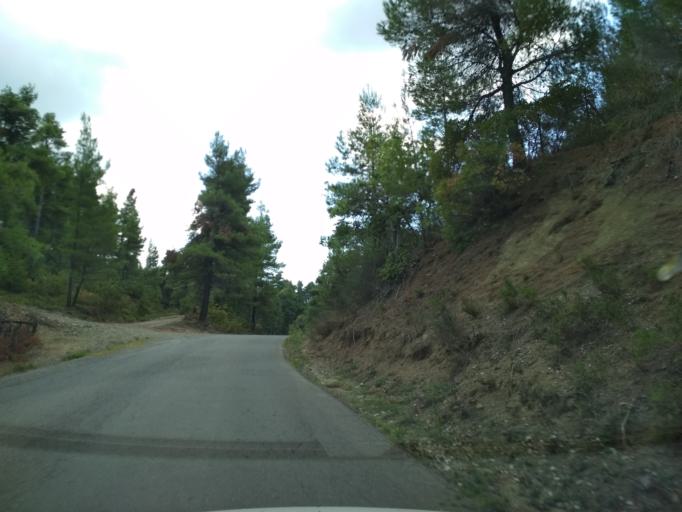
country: GR
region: Central Greece
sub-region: Nomos Evvoias
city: Roviai
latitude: 38.8542
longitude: 23.2887
